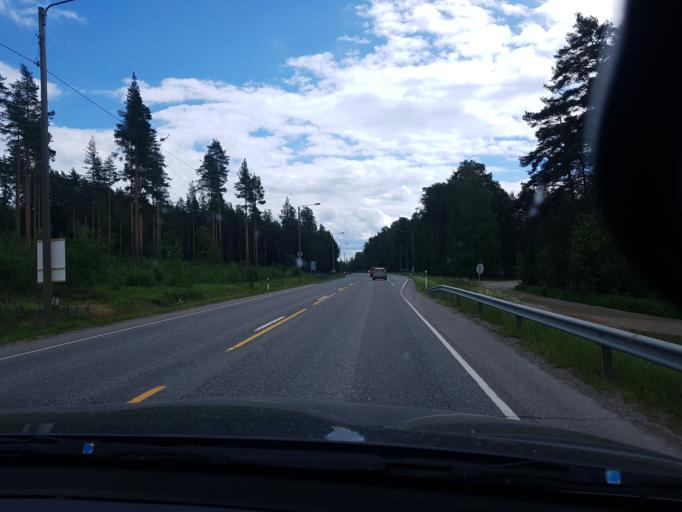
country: FI
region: Pirkanmaa
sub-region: Tampere
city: Paelkaene
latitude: 61.3005
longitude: 24.3037
